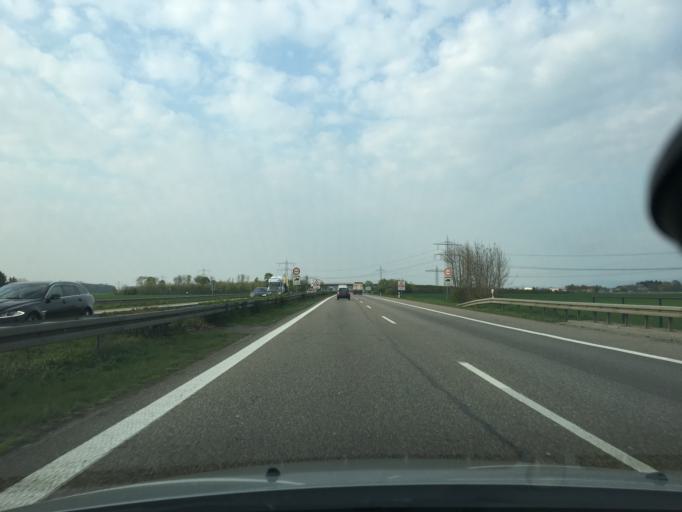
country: DE
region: Baden-Wuerttemberg
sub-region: Freiburg Region
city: Herbolzheim
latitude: 48.2320
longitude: 7.7510
